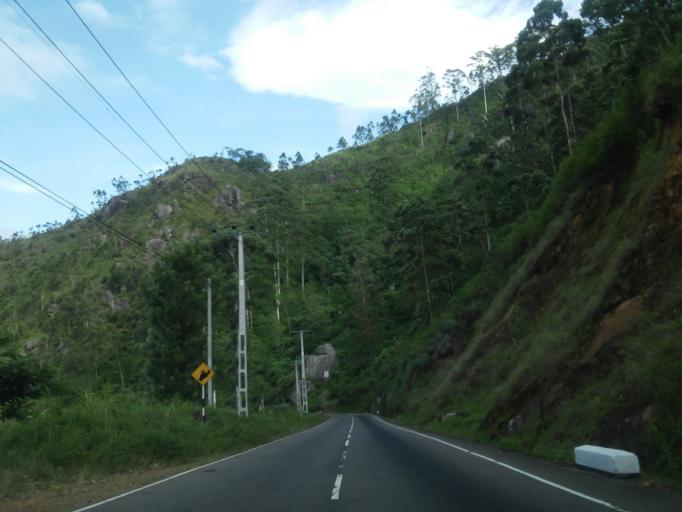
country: LK
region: Uva
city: Haputale
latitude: 6.7619
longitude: 80.9506
